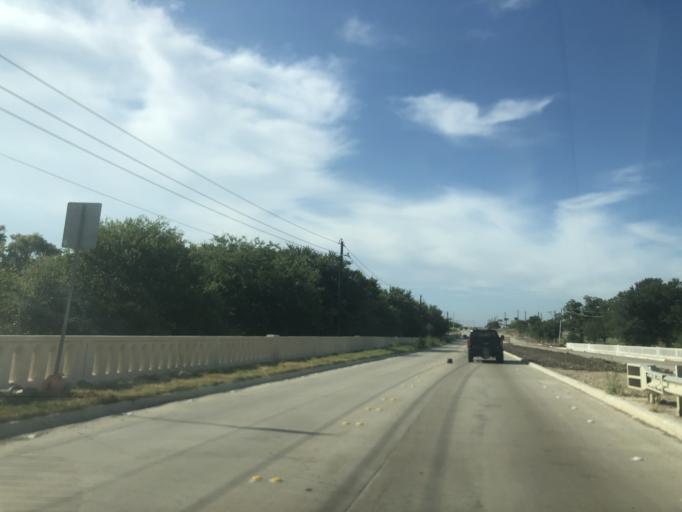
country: US
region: Texas
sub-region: Denton County
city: Justin
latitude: 33.0773
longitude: -97.2958
